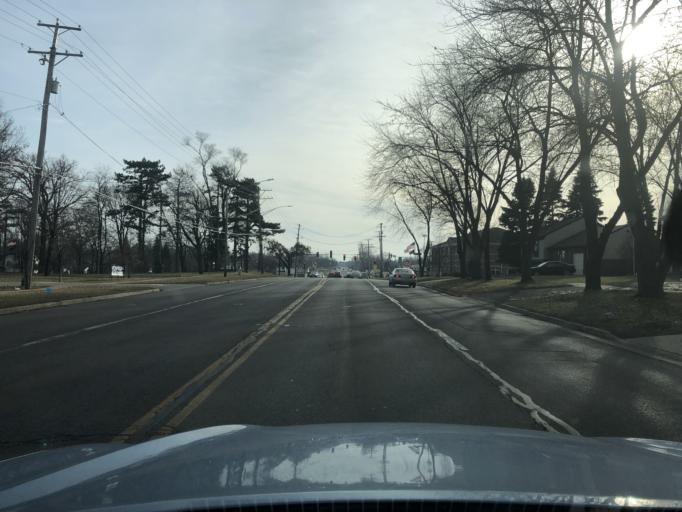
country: US
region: Illinois
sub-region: DuPage County
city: Glendale Heights
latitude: 41.9191
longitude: -88.0814
